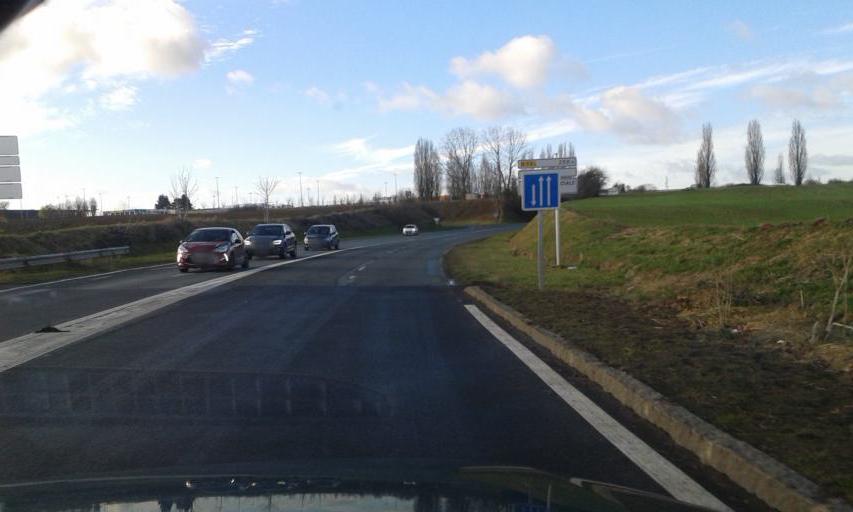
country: FR
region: Picardie
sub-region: Departement de l'Oise
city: Venette
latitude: 49.4081
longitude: 2.7903
